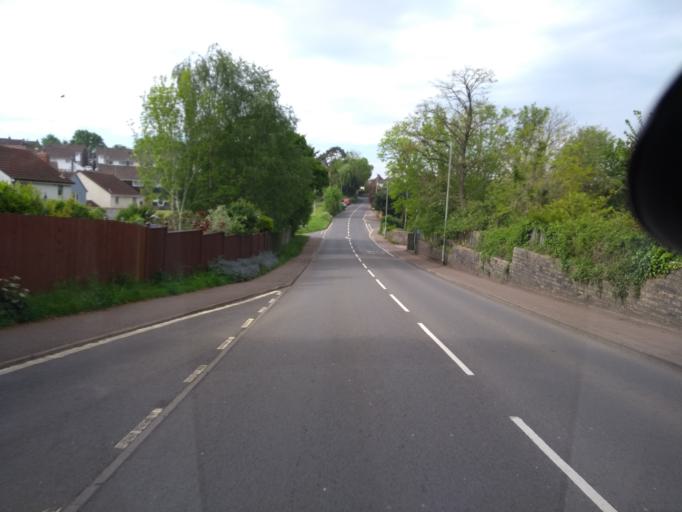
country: GB
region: England
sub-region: Devon
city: Axminster
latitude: 50.7765
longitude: -3.0022
